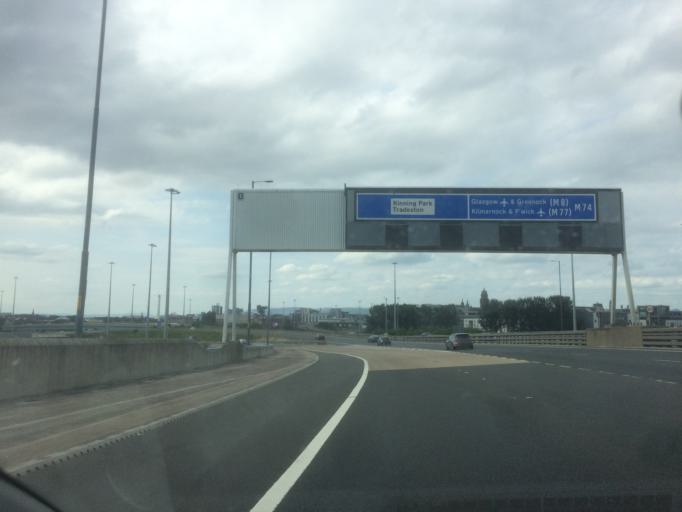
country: GB
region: Scotland
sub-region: Glasgow City
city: Glasgow
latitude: 55.8494
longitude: -4.2648
